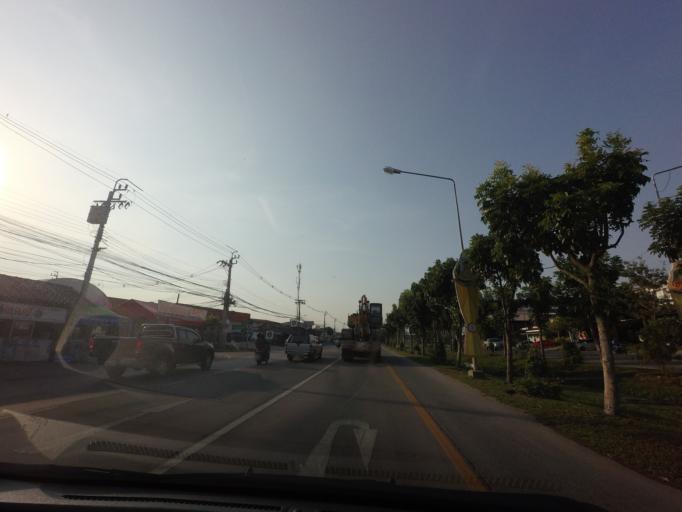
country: TH
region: Bangkok
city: Taling Chan
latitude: 13.7655
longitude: 100.4265
